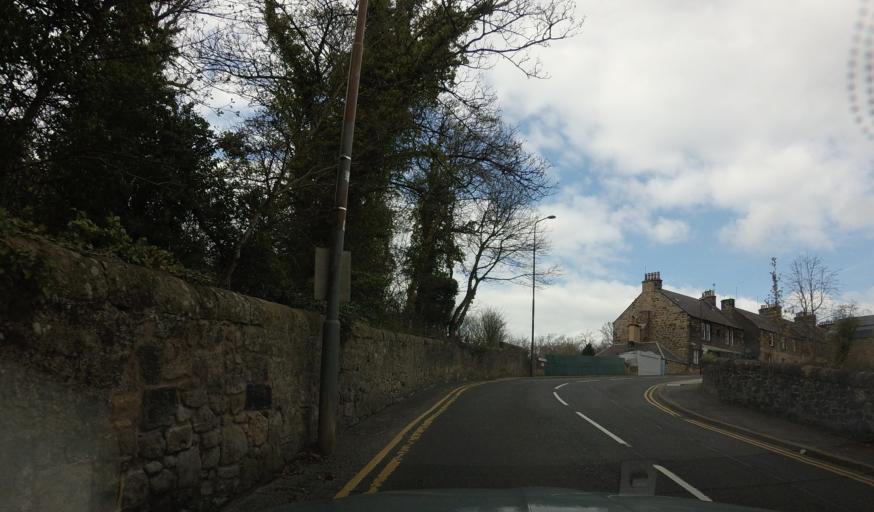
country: GB
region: Scotland
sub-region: Midlothian
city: Gorebridge
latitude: 55.8403
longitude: -3.0484
